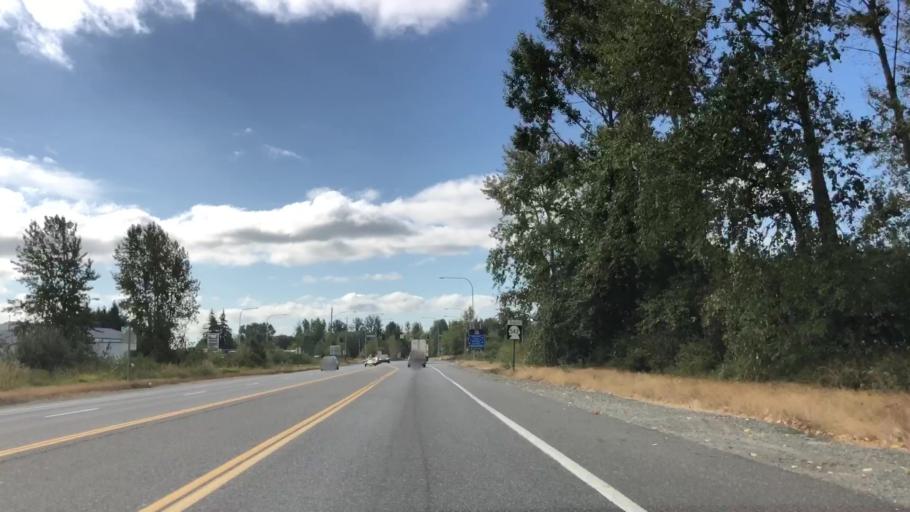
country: US
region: Washington
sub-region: Whatcom County
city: Blaine
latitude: 48.9924
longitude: -122.7350
